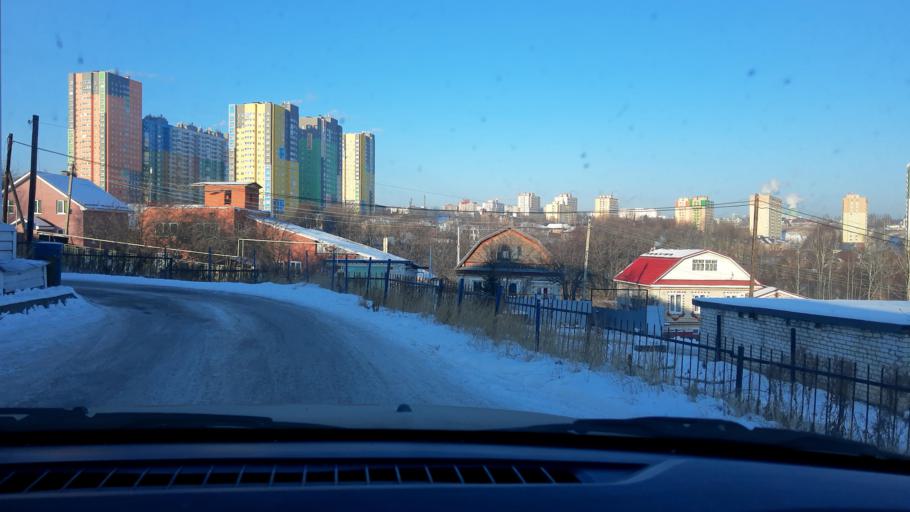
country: RU
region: Nizjnij Novgorod
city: Afonino
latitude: 56.2738
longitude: 44.0913
